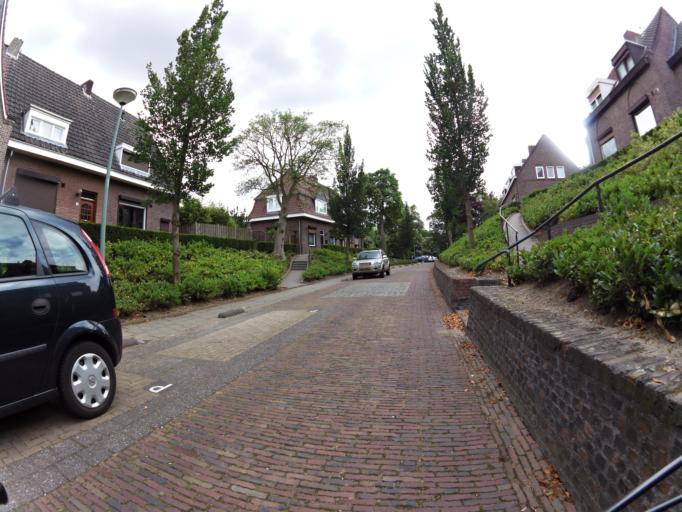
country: NL
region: Limburg
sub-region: Gemeente Brunssum
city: Brunssum
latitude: 50.9359
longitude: 5.9641
